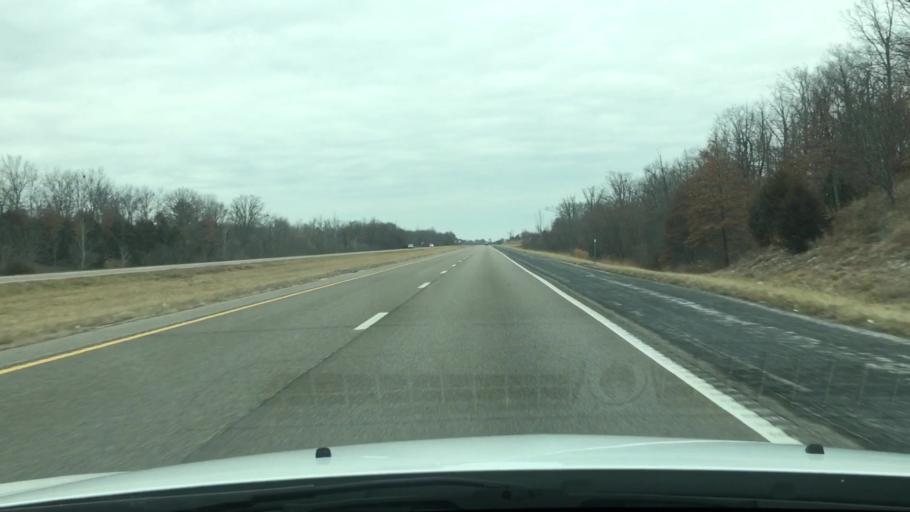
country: US
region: Missouri
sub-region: Callaway County
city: Fulton
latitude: 38.9845
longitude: -91.8939
